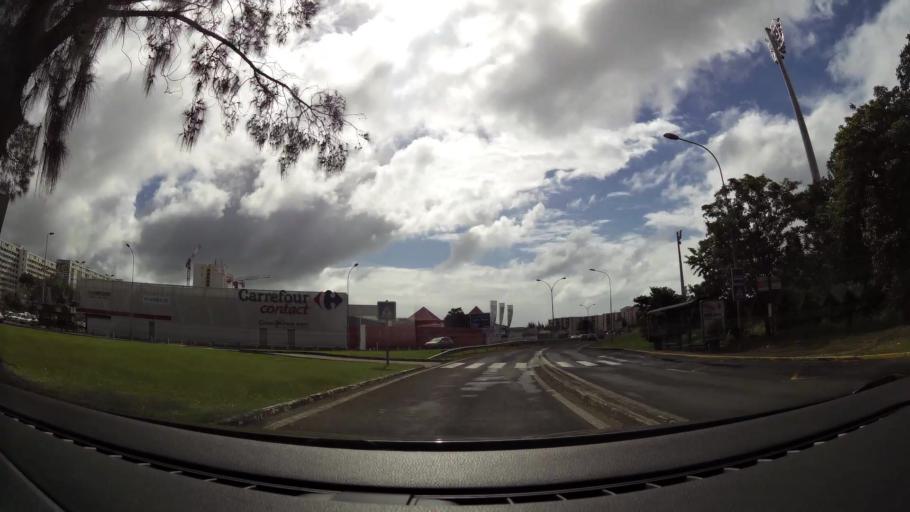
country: GP
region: Guadeloupe
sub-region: Guadeloupe
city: Pointe-a-Pitre
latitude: 16.2527
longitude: -61.5421
